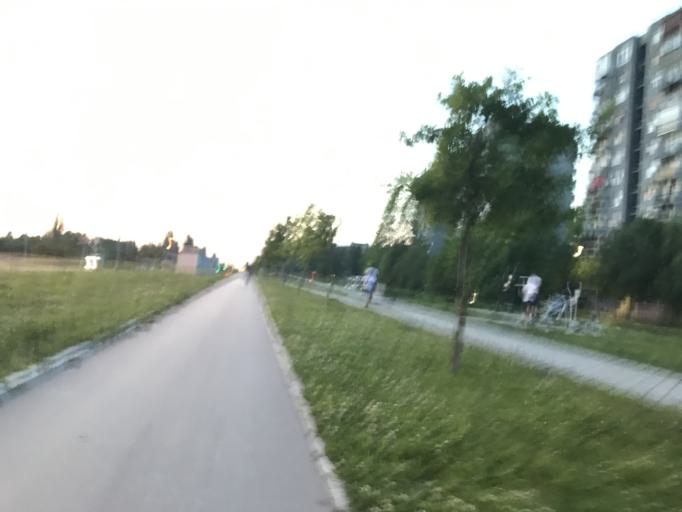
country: RS
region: Autonomna Pokrajina Vojvodina
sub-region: Juznobacki Okrug
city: Novi Sad
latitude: 45.2627
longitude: 19.8073
